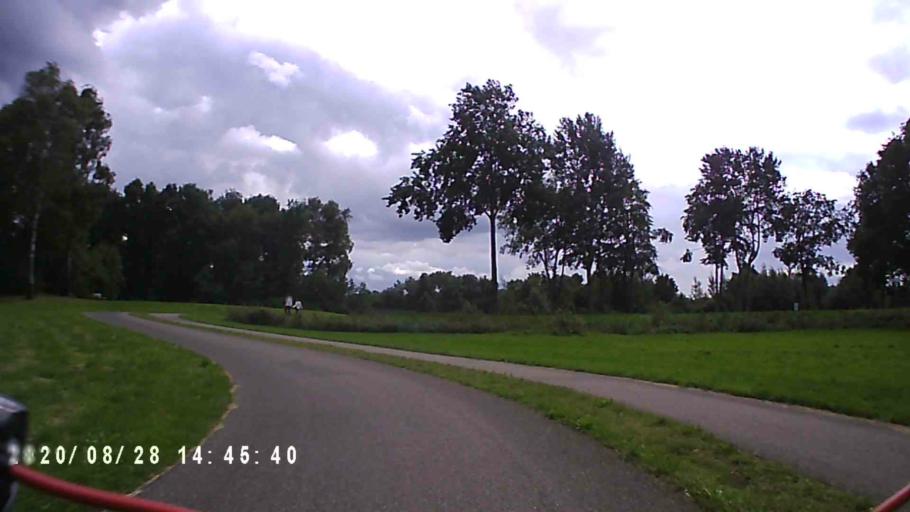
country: NL
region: Groningen
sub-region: Gemeente Groningen
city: Groningen
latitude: 53.1747
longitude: 6.5539
